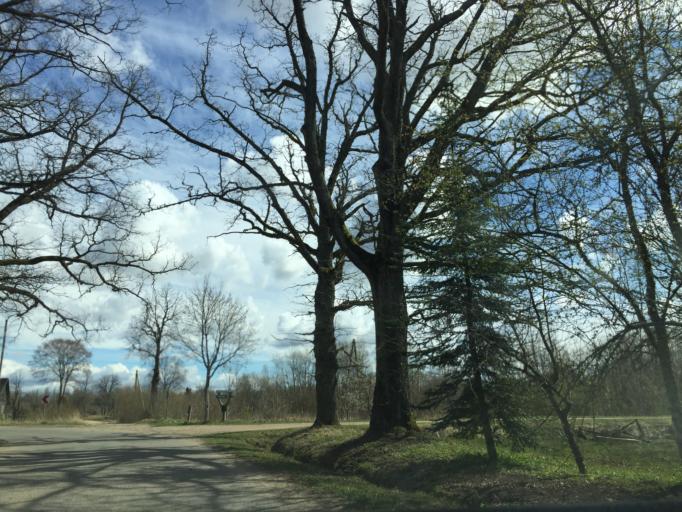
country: LV
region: Limbazu Rajons
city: Limbazi
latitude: 57.6113
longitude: 24.6670
